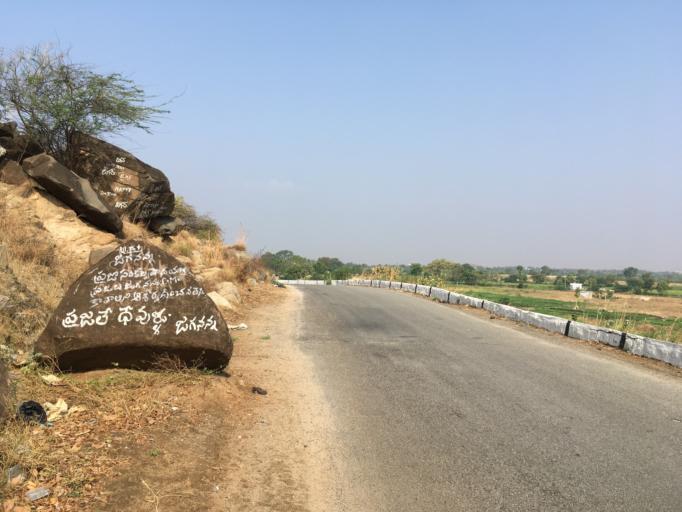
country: IN
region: Andhra Pradesh
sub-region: Anantapur
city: Puttaparthi
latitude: 14.1857
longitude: 77.7805
